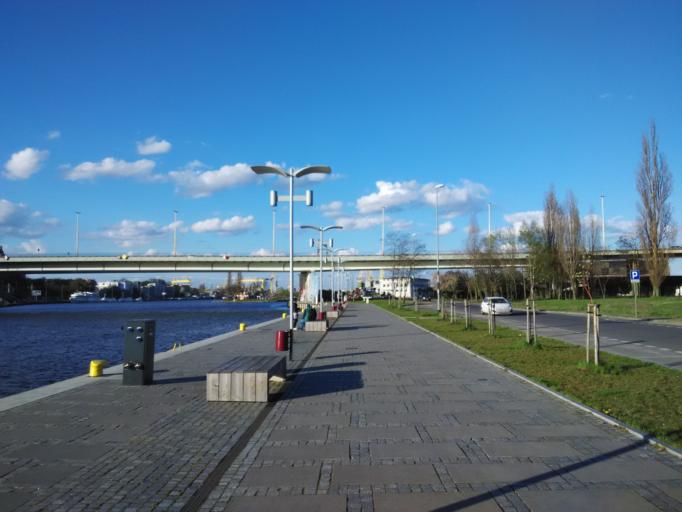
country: PL
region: West Pomeranian Voivodeship
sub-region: Szczecin
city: Szczecin
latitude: 53.4239
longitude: 14.5650
